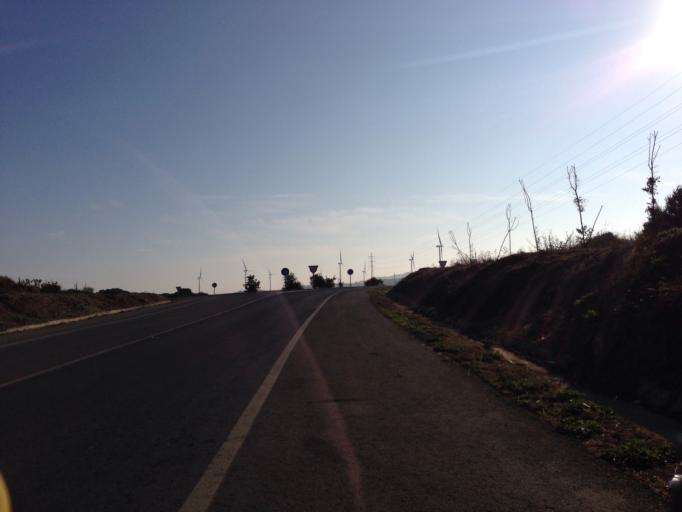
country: ES
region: Andalusia
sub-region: Provincia de Cadiz
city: Conil de la Frontera
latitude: 36.2923
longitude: -6.0566
